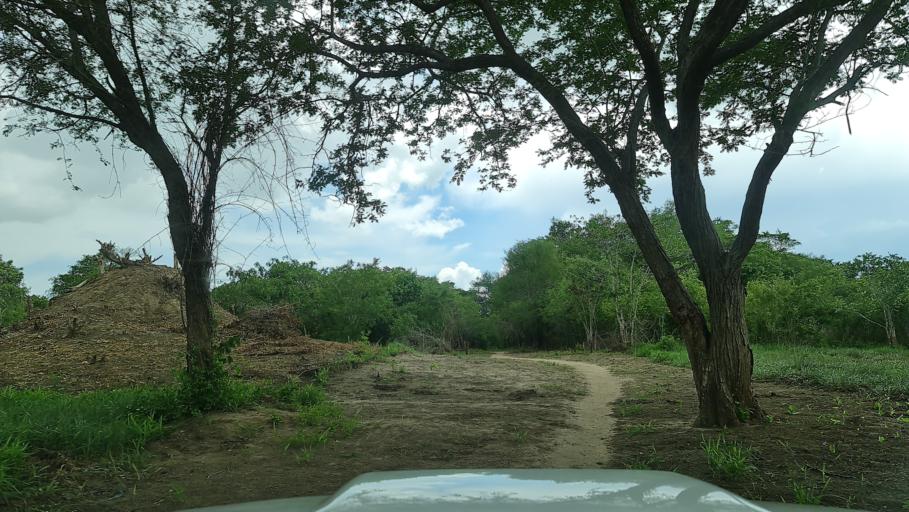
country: MZ
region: Nampula
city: Ilha de Mocambique
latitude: -15.5018
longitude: 40.1581
